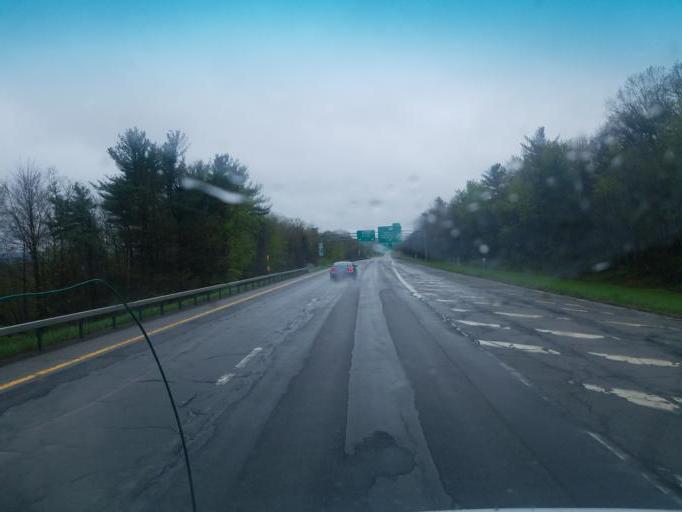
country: US
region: New York
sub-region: Chautauqua County
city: Lakewood
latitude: 42.1487
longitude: -79.3642
